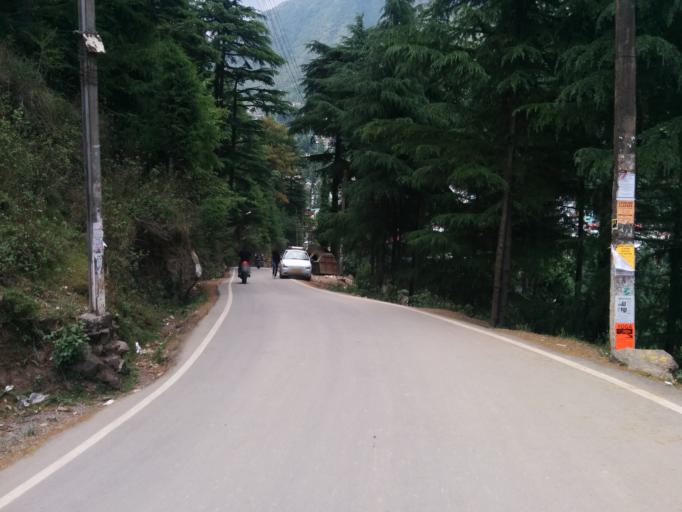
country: IN
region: Himachal Pradesh
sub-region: Kangra
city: Dharmsala
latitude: 32.2407
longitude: 76.3323
